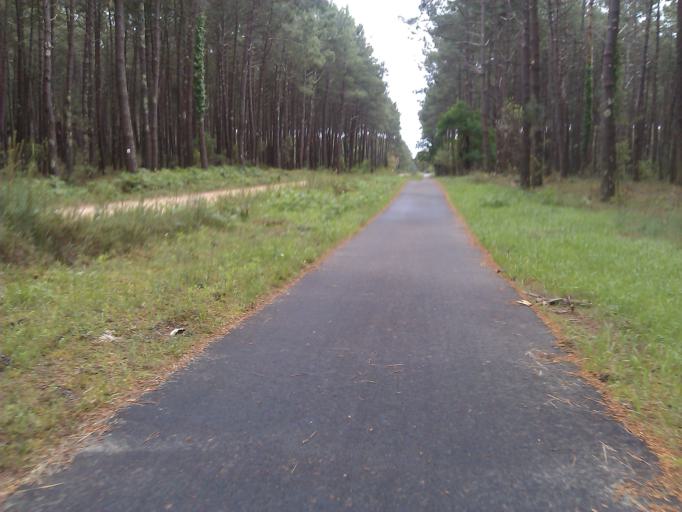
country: FR
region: Aquitaine
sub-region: Departement des Landes
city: Vielle-Saint-Girons
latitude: 43.9324
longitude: -1.3527
